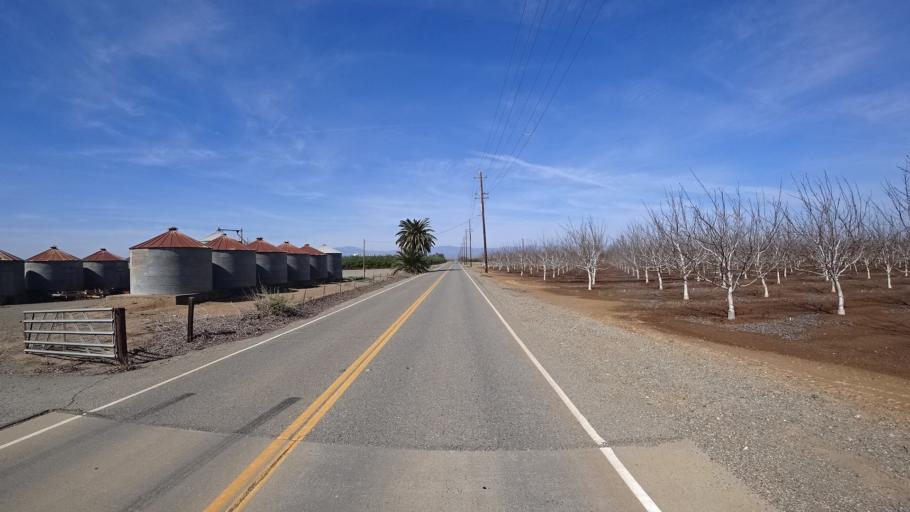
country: US
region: California
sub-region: Glenn County
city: Willows
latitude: 39.5388
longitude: -122.2515
